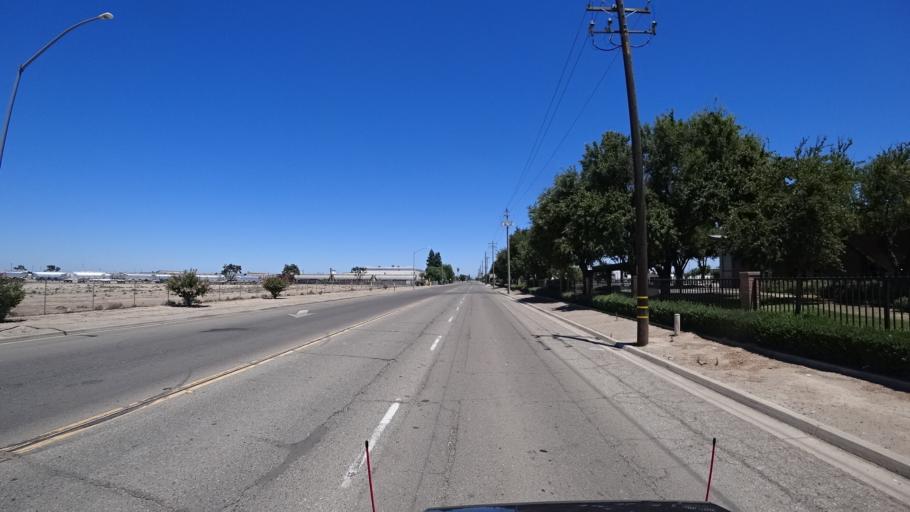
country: US
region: California
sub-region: Fresno County
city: Fresno
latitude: 36.6944
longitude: -119.7456
